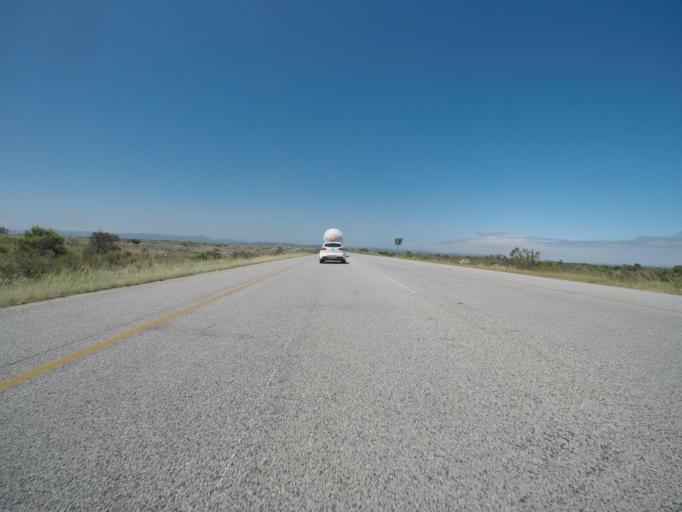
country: ZA
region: Eastern Cape
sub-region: Cacadu District Municipality
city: Jeffrey's Bay
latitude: -33.9560
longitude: 24.9619
